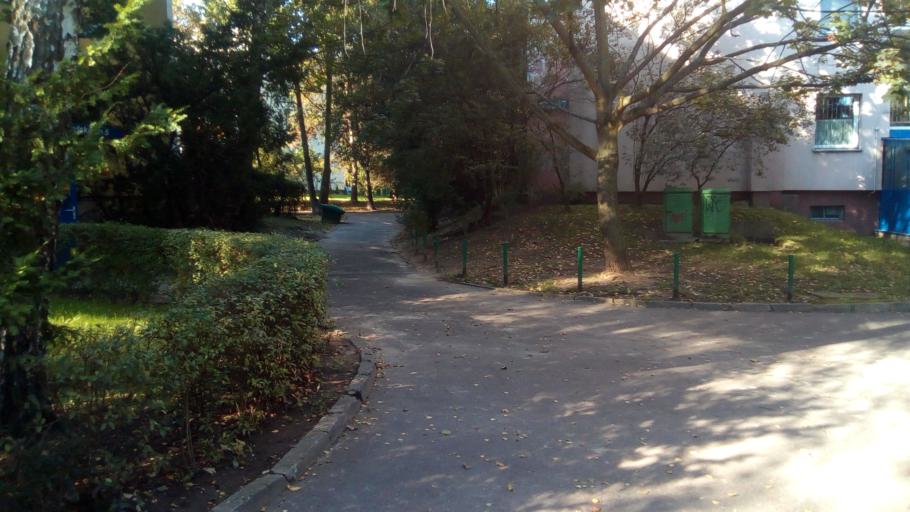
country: PL
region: Masovian Voivodeship
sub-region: Warszawa
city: Ursynow
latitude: 52.1584
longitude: 21.0540
